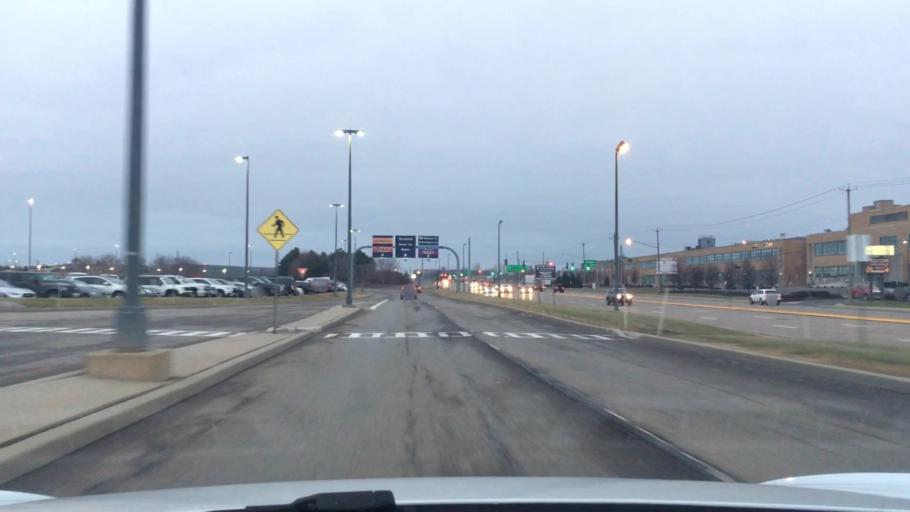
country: US
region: New York
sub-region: Erie County
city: Williamsville
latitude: 42.9329
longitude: -78.7261
